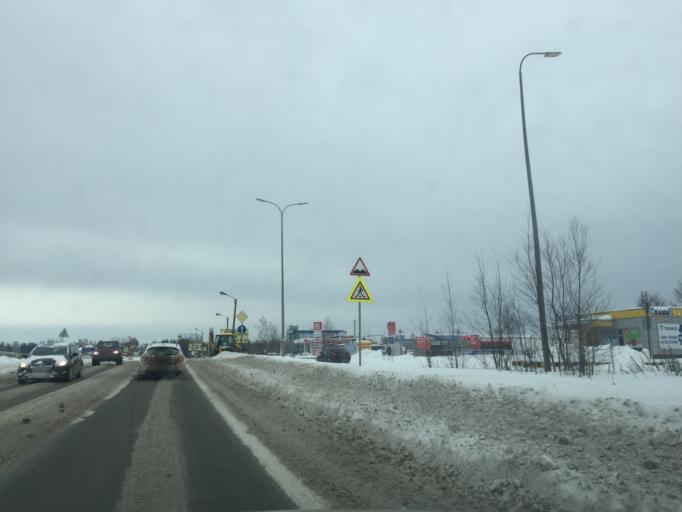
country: RU
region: Leningrad
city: Yanino Vtoroye
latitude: 59.9447
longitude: 30.5923
